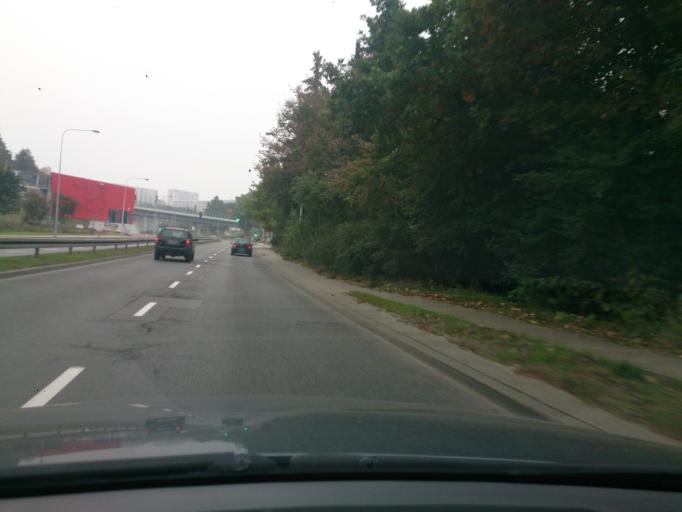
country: PL
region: Pomeranian Voivodeship
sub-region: Powiat gdanski
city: Kowale
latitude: 54.3665
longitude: 18.5717
